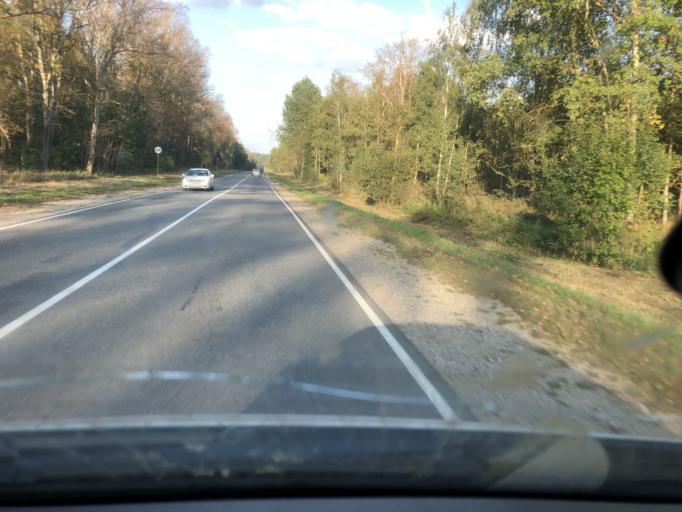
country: RU
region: Kaluga
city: Peremyshl'
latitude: 54.2192
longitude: 36.0241
